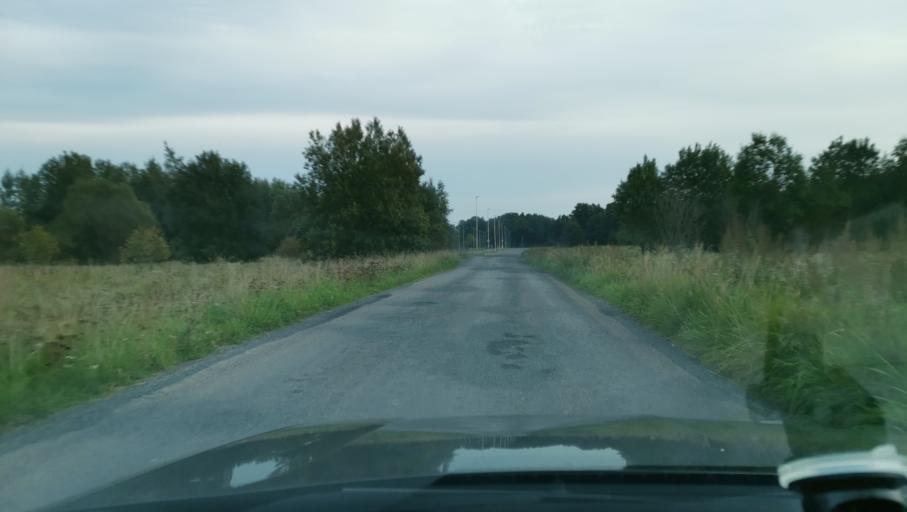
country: EE
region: Harju
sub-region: Saue vald
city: Laagri
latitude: 59.4206
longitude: 24.6285
